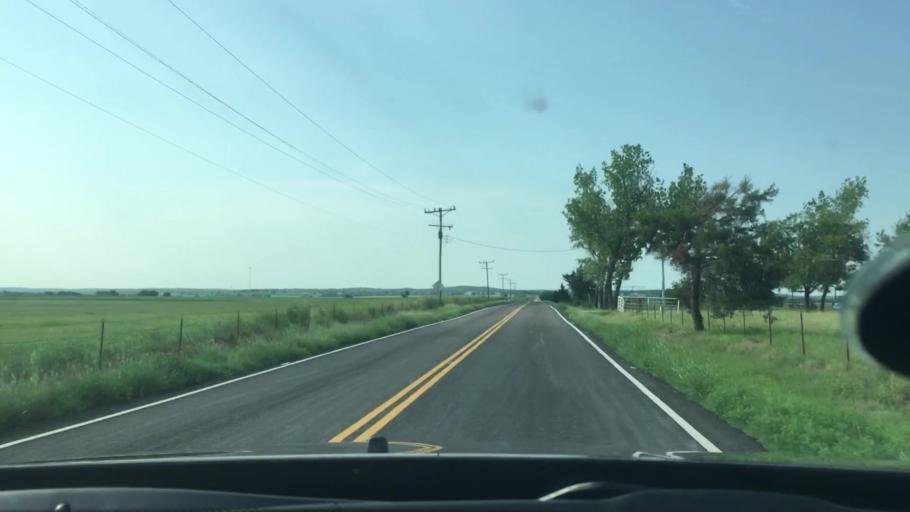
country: US
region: Oklahoma
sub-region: Bryan County
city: Durant
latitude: 34.1185
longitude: -96.4877
